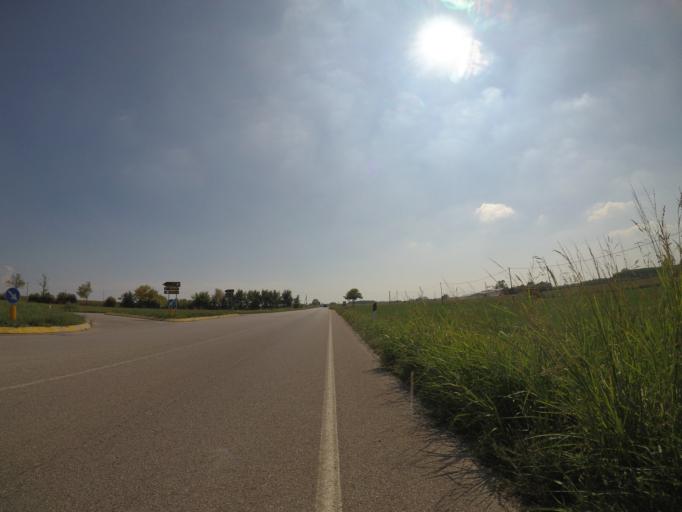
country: IT
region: Friuli Venezia Giulia
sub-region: Provincia di Udine
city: Pocenia
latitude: 45.8228
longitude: 13.1009
